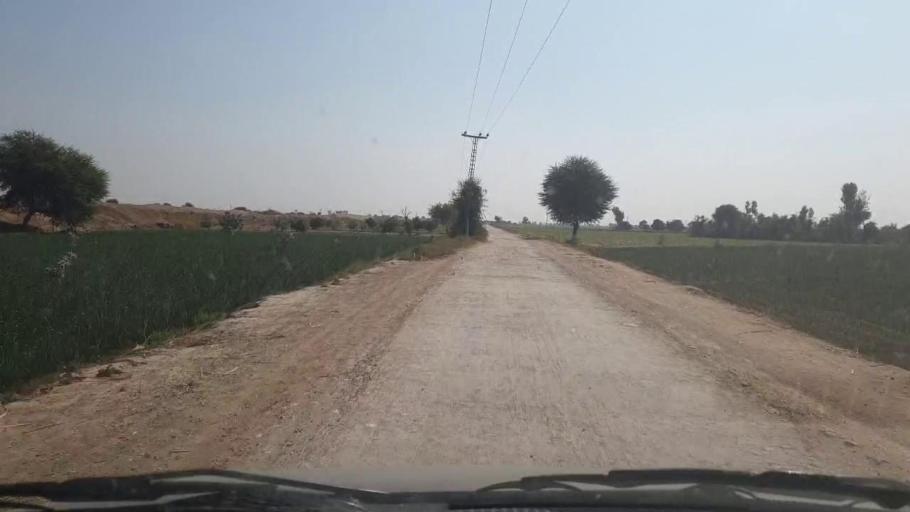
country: PK
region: Sindh
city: Samaro
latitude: 25.2550
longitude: 69.3539
